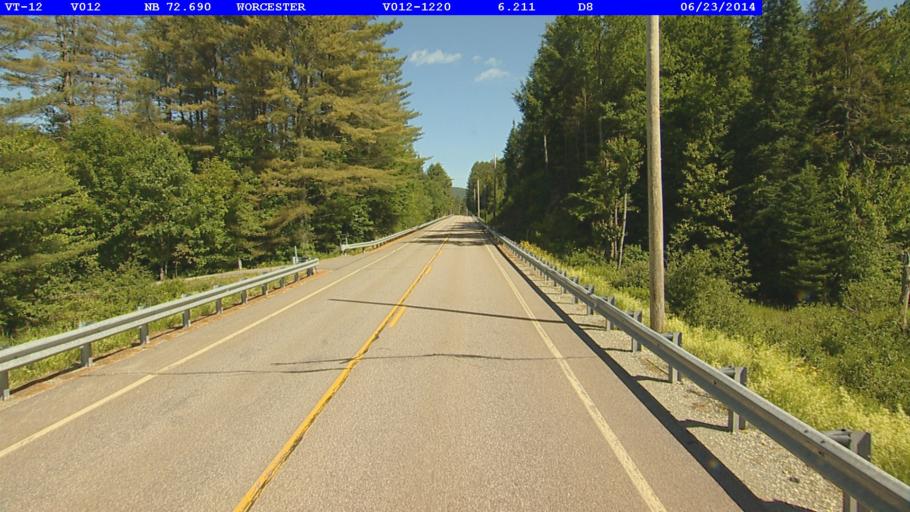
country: US
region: Vermont
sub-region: Lamoille County
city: Morrisville
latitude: 44.4311
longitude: -72.5337
